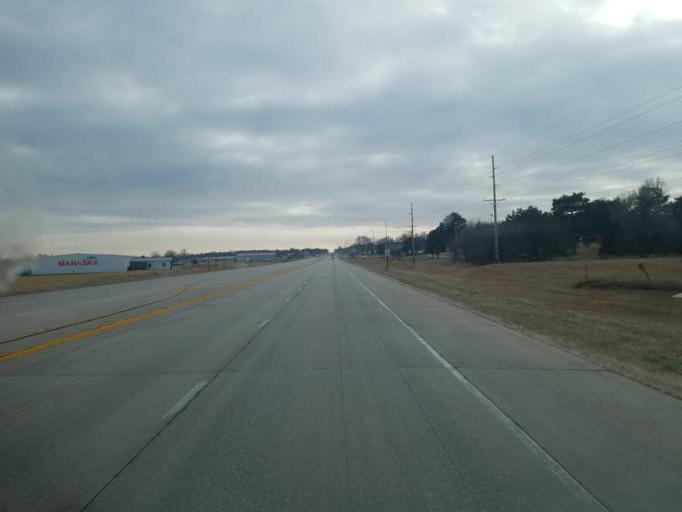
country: US
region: Nebraska
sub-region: Madison County
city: Norfolk
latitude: 42.0566
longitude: -97.4267
